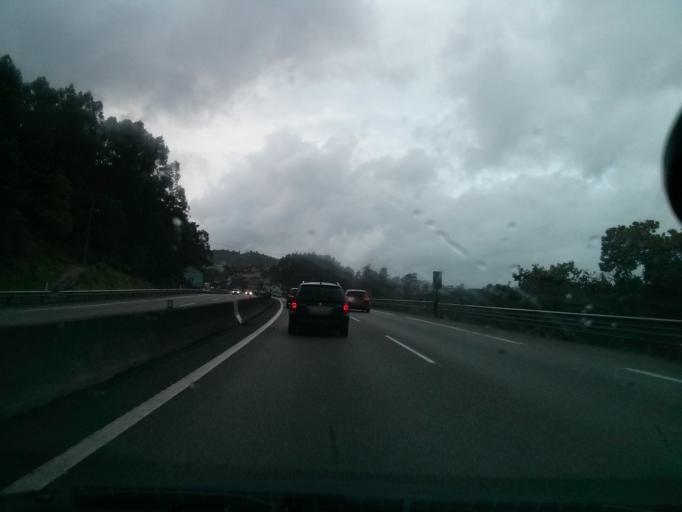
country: ES
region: Galicia
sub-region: Provincia de Pontevedra
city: Porrino
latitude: 42.1923
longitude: -8.6407
